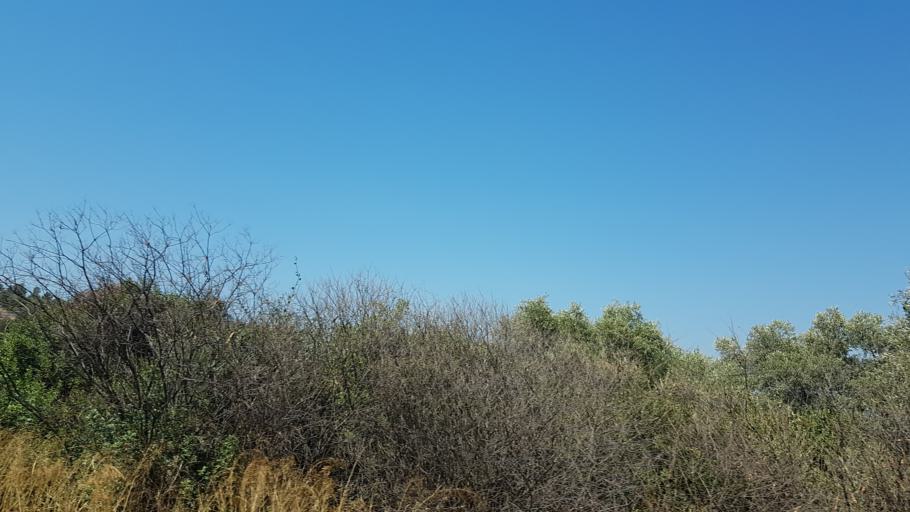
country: TR
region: Mugla
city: Kiulukioi
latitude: 37.1248
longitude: 27.5436
